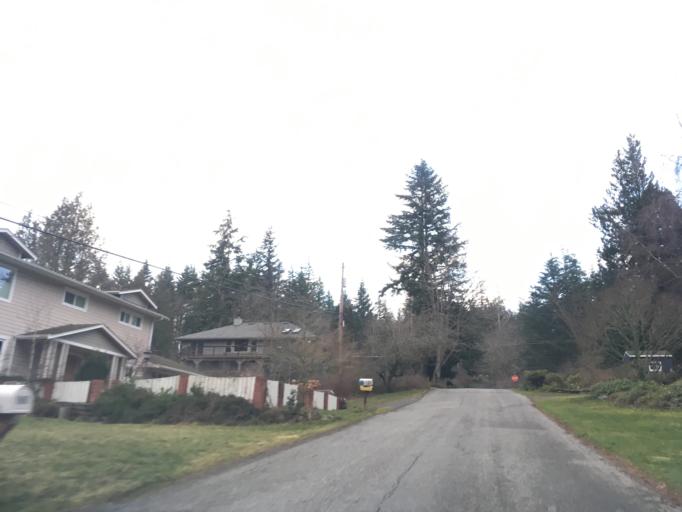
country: US
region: Washington
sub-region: Whatcom County
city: Bellingham
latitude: 48.7203
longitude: -122.4658
